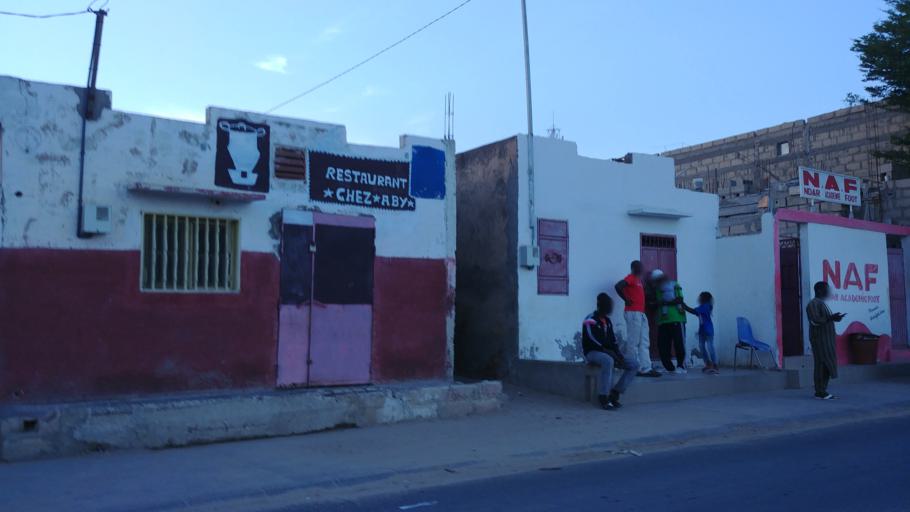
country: SN
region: Saint-Louis
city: Saint-Louis
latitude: 16.0086
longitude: -16.4886
